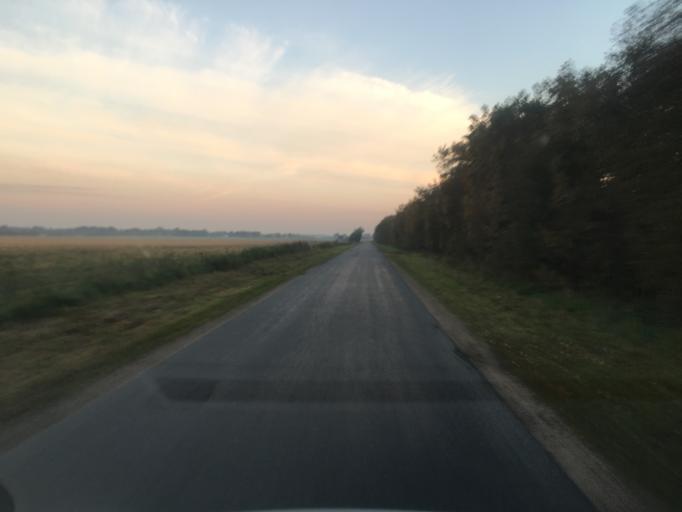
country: DK
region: South Denmark
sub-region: Tonder Kommune
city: Logumkloster
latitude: 54.9896
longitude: 9.0513
